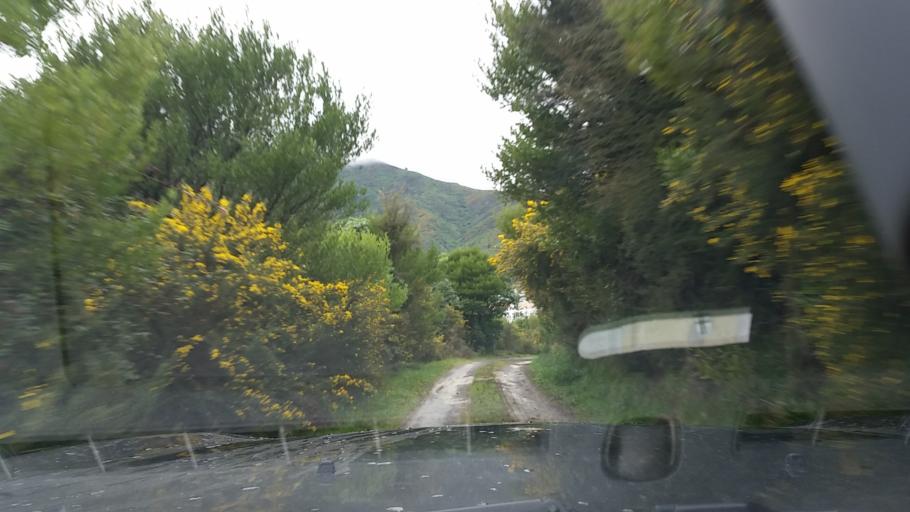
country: NZ
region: Marlborough
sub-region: Marlborough District
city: Picton
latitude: -41.2641
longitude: 174.0372
